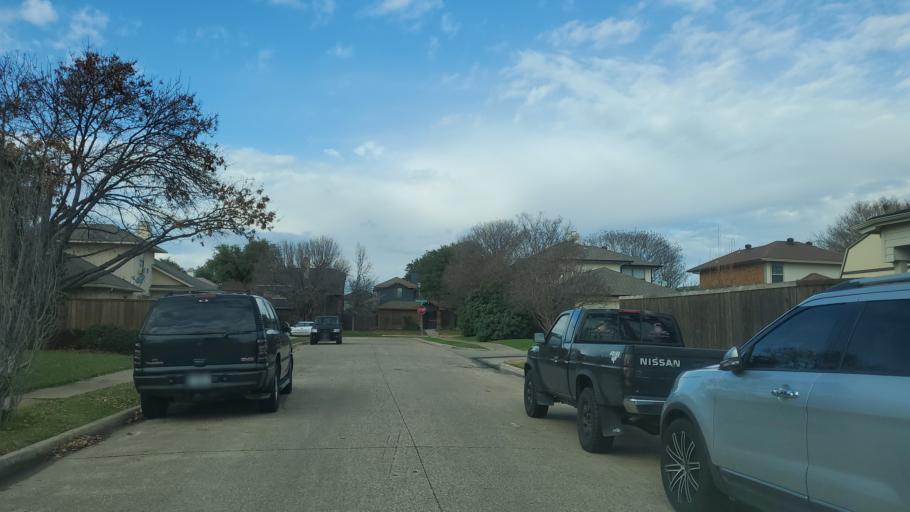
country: US
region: Texas
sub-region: Dallas County
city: Carrollton
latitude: 32.9955
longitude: -96.8997
